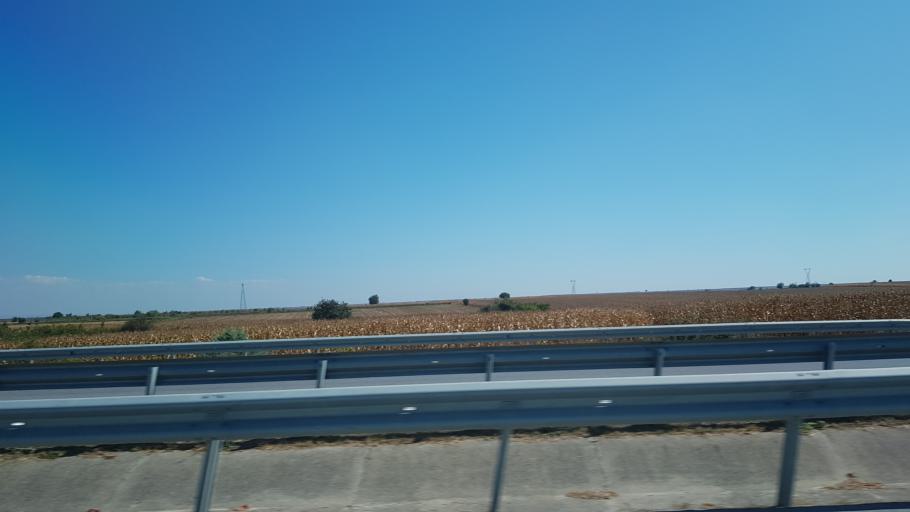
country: TR
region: Kirklareli
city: Inece
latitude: 41.5981
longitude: 27.1611
